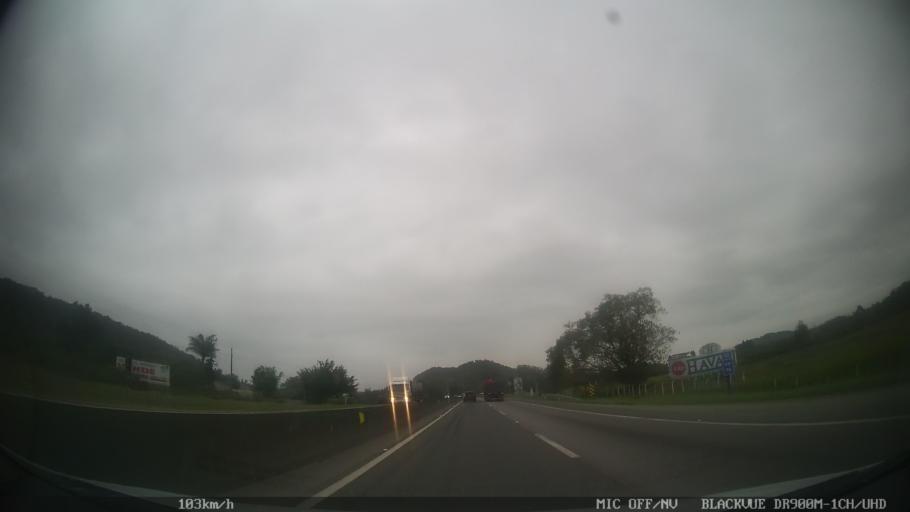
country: BR
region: Santa Catarina
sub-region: Barra Velha
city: Barra Velha
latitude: -26.5622
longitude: -48.7194
